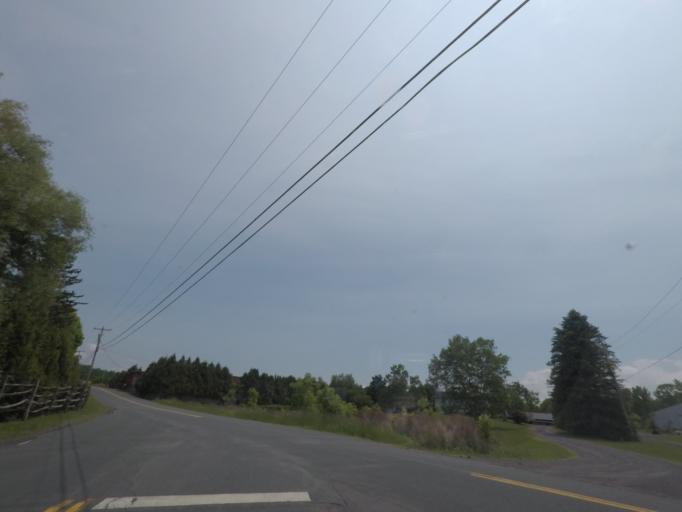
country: US
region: New York
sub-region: Columbia County
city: Niverville
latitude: 42.4757
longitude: -73.6951
